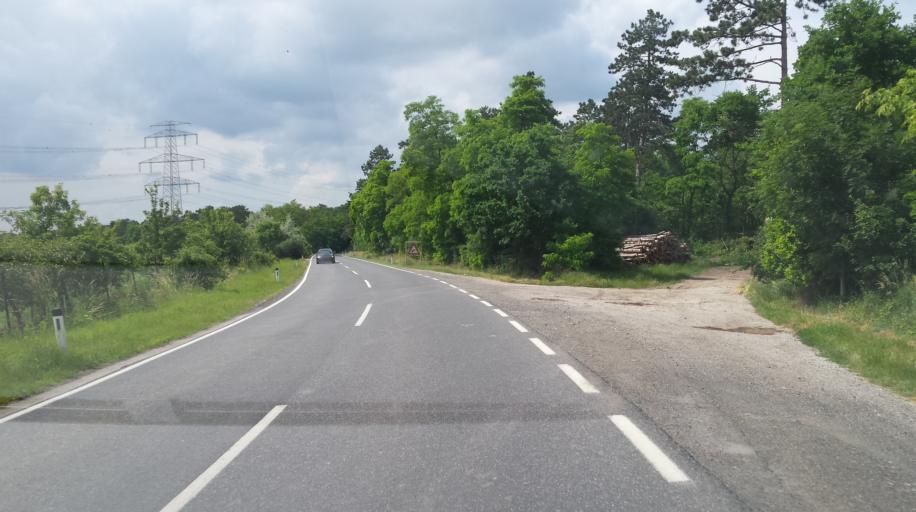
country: AT
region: Lower Austria
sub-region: Politischer Bezirk Ganserndorf
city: Aderklaa
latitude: 48.3038
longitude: 16.5440
